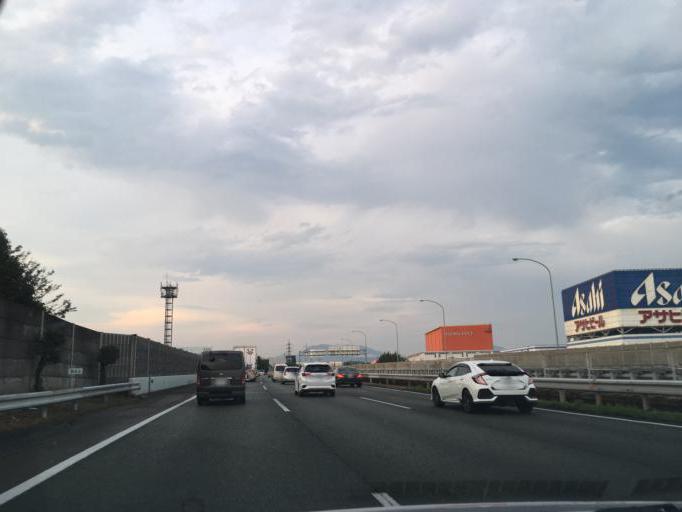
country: JP
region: Saga Prefecture
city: Tosu
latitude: 33.4073
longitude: 130.5379
